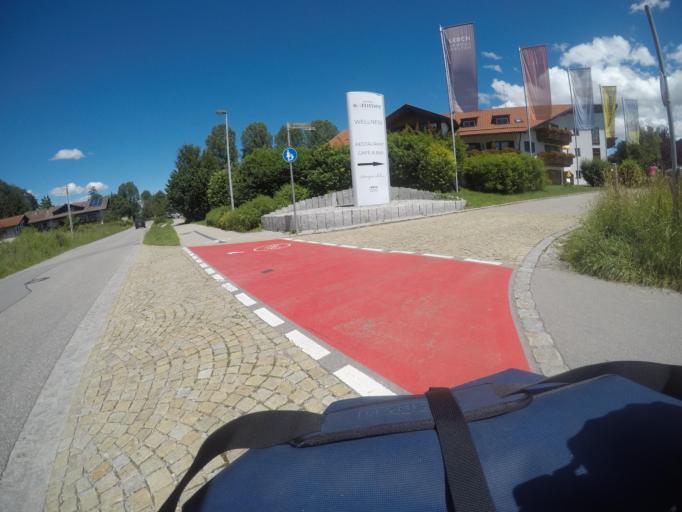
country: DE
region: Bavaria
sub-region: Swabia
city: Fuessen
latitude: 47.5796
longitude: 10.7090
